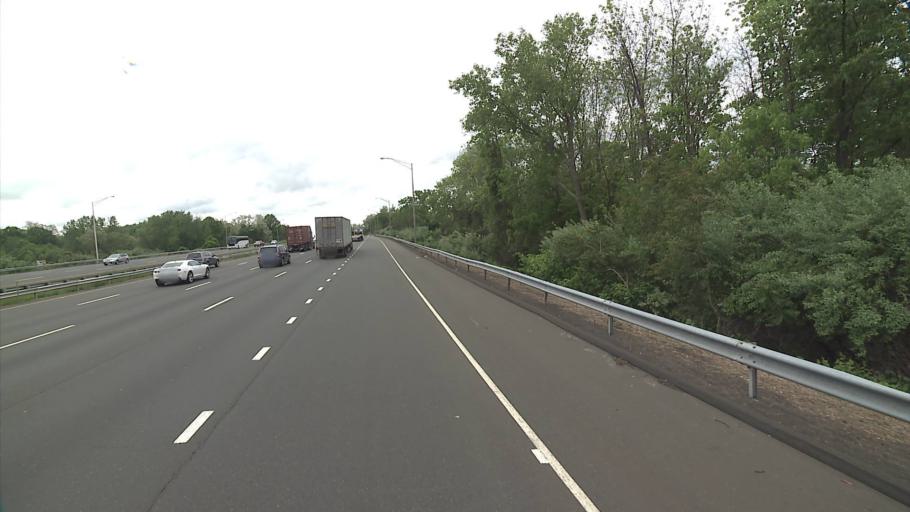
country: US
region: Connecticut
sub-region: New Haven County
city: North Haven
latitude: 41.3711
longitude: -72.8699
